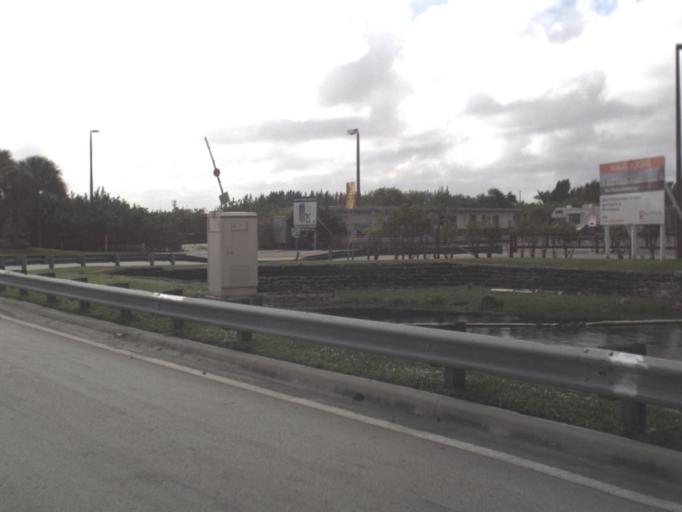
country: US
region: Florida
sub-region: Miami-Dade County
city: Virginia Gardens
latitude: 25.8031
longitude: -80.3051
